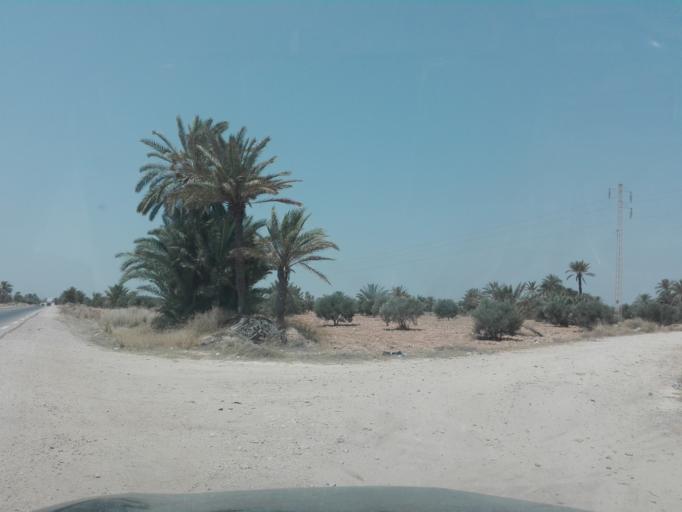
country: TN
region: Safaqis
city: Al Qarmadah
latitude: 34.6582
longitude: 11.1015
